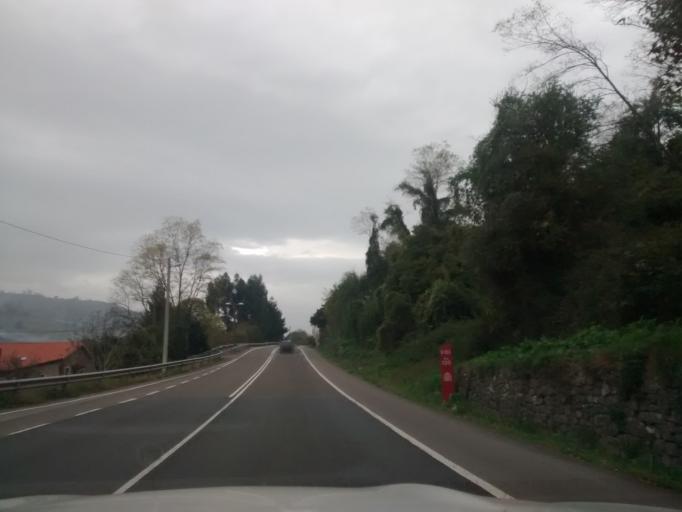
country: ES
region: Cantabria
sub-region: Provincia de Cantabria
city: Corvera
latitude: 43.2531
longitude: -3.9482
